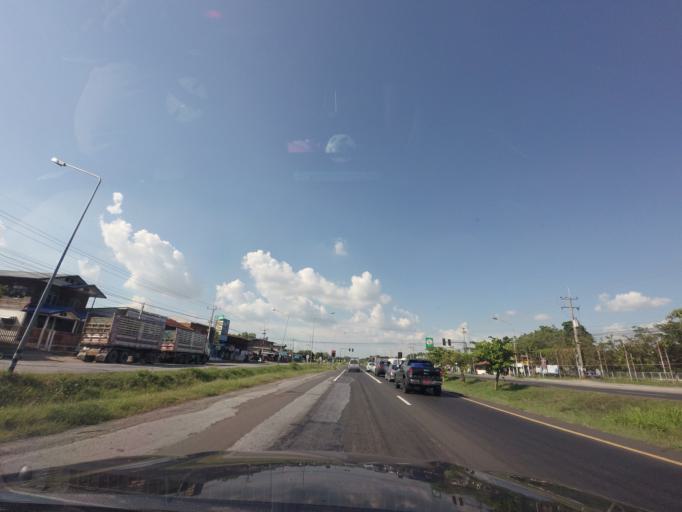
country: TH
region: Nakhon Ratchasima
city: Bua Lai
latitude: 15.6384
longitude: 102.5692
